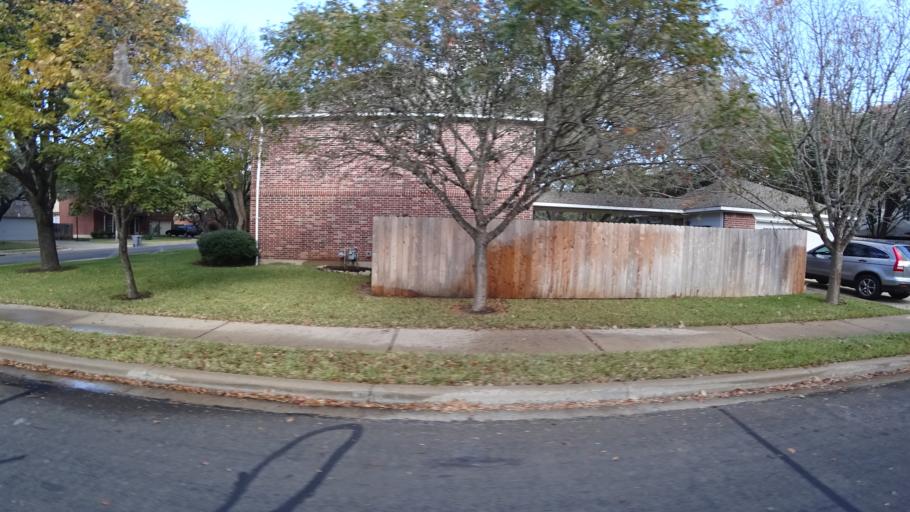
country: US
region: Texas
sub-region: Travis County
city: Shady Hollow
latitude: 30.1818
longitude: -97.8599
